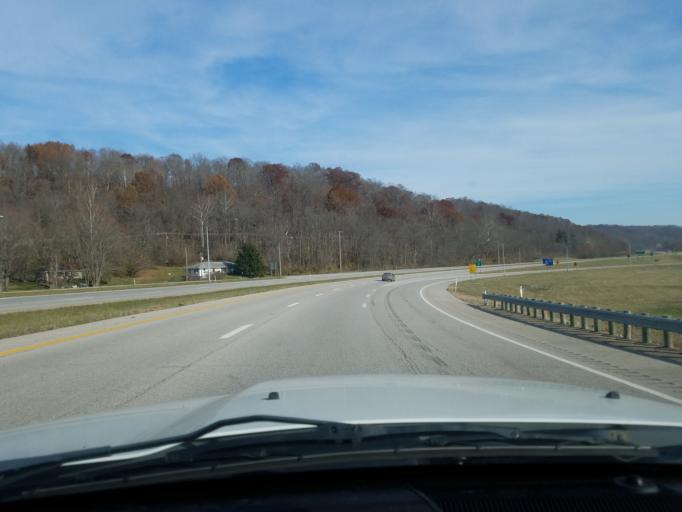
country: US
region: Ohio
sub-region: Athens County
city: Athens
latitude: 39.3349
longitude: -82.0331
